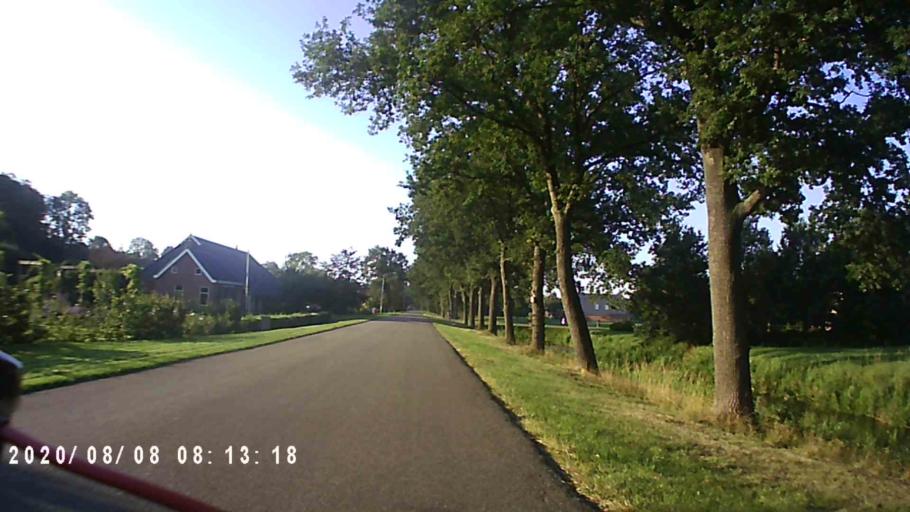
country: NL
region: Groningen
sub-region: Gemeente Leek
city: Leek
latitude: 53.1006
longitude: 6.3401
